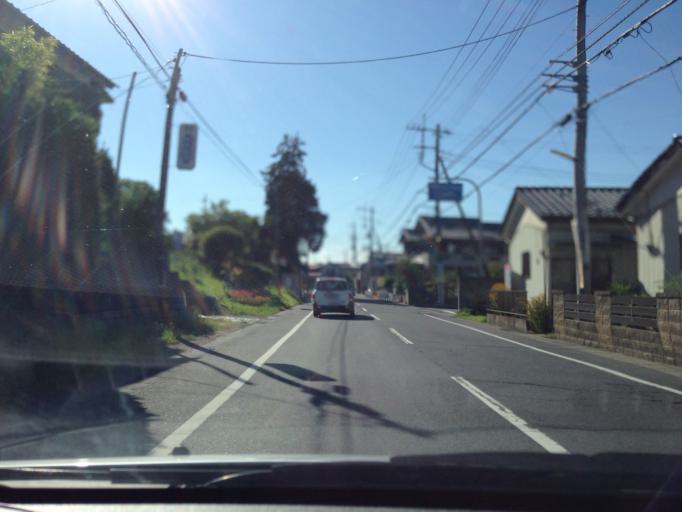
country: JP
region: Ibaraki
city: Naka
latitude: 36.0750
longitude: 140.1927
